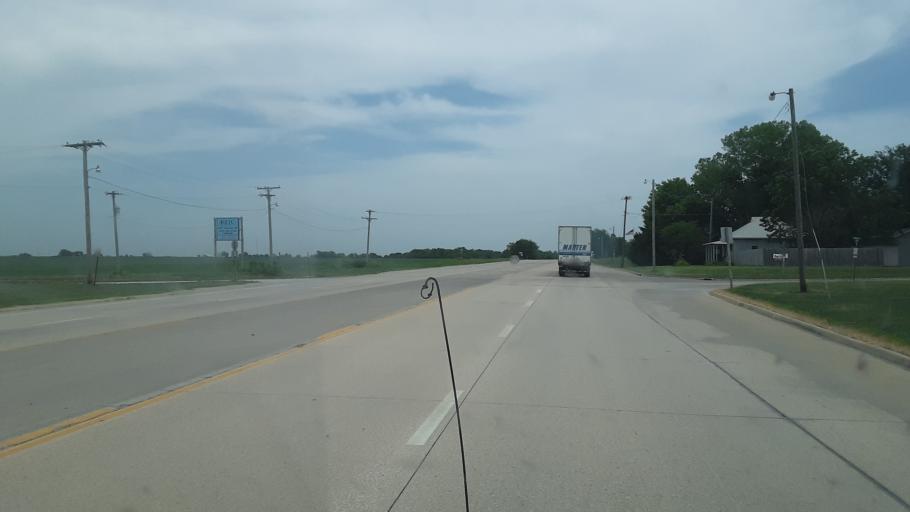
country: US
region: Kansas
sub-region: Allen County
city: Iola
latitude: 37.9221
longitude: -95.2998
